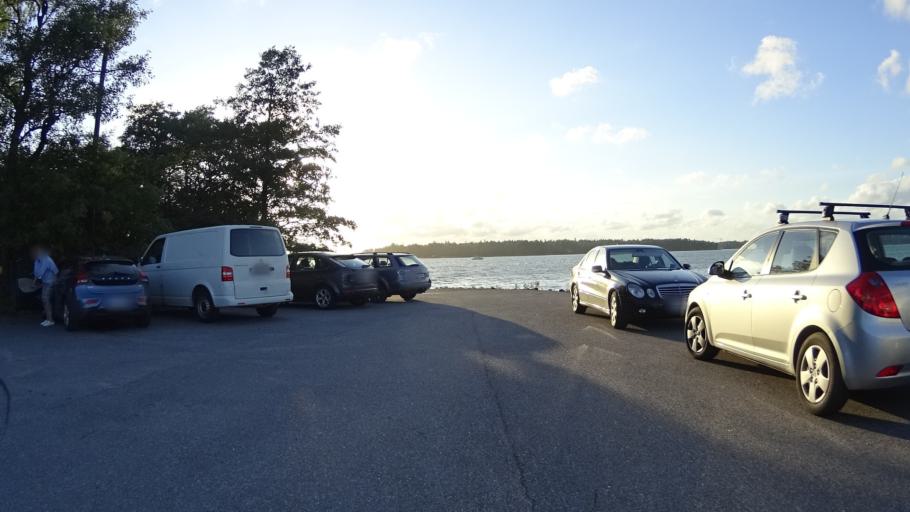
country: FI
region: Uusimaa
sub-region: Helsinki
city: Helsinki
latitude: 60.1719
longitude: 24.9005
